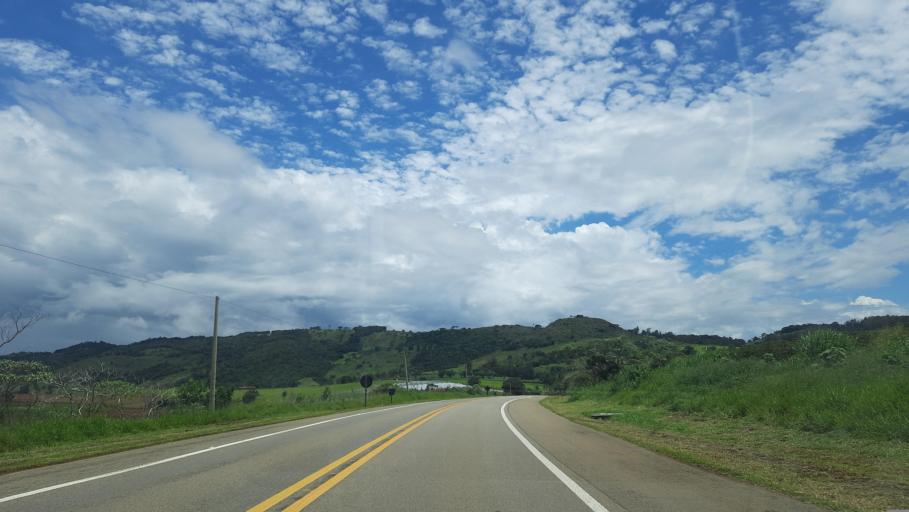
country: BR
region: Sao Paulo
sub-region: Vargem Grande Do Sul
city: Vargem Grande do Sul
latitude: -21.8156
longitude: -46.7850
